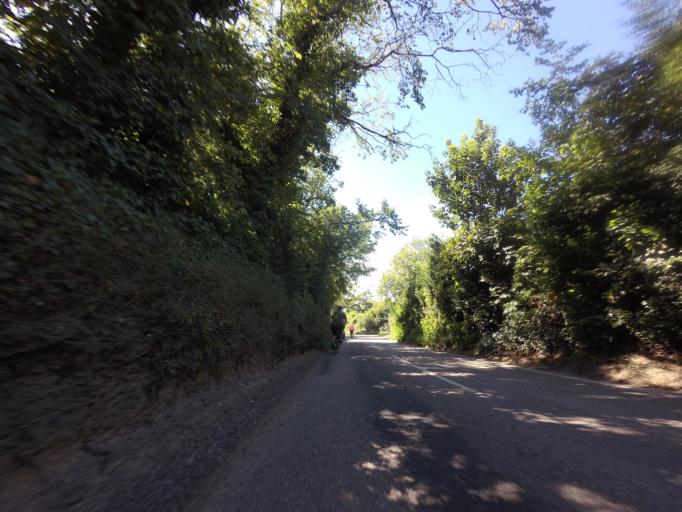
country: GB
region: England
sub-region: Kent
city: Birchington-on-Sea
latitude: 51.3351
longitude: 1.3291
